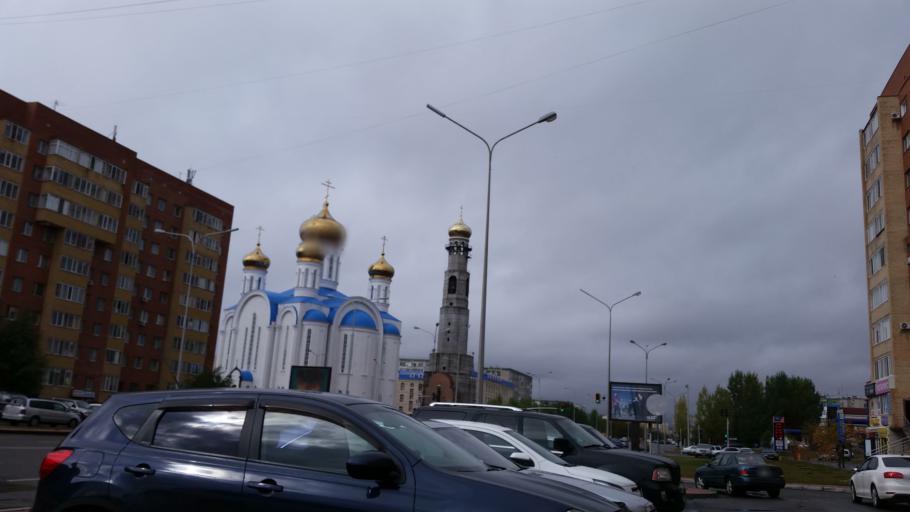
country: KZ
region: Astana Qalasy
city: Astana
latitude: 51.1484
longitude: 71.4838
